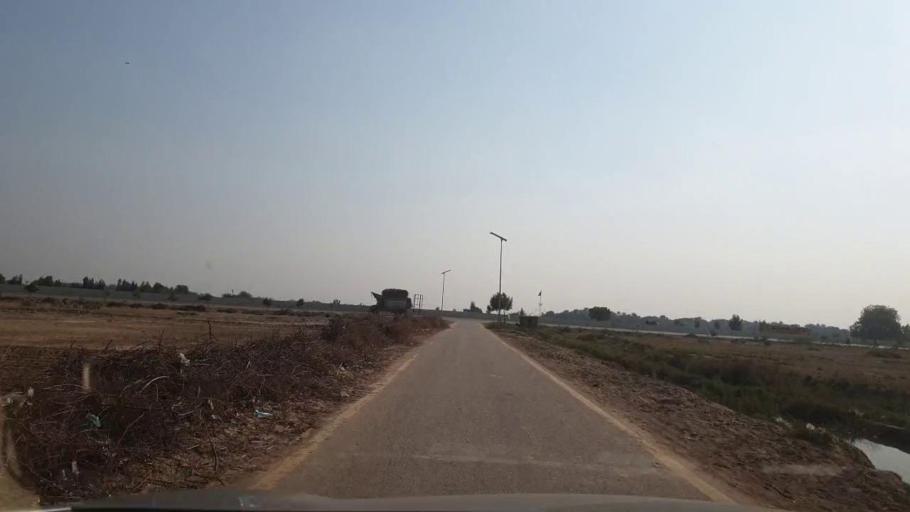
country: PK
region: Sindh
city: Tando Allahyar
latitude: 25.4938
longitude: 68.8660
